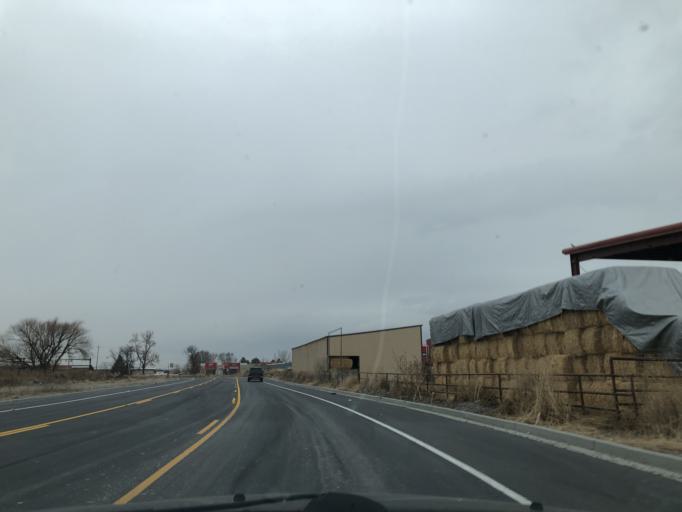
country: US
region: Utah
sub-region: Cache County
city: Nibley
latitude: 41.6947
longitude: -111.8588
